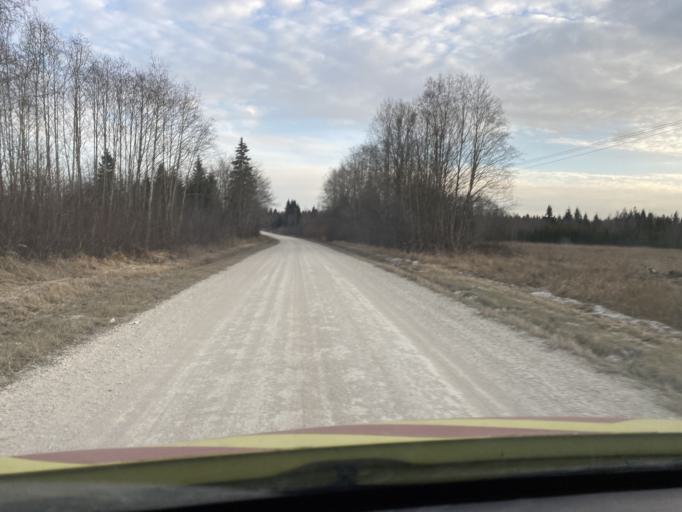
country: EE
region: Jogevamaa
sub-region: Poltsamaa linn
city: Poltsamaa
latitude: 58.5869
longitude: 26.0363
